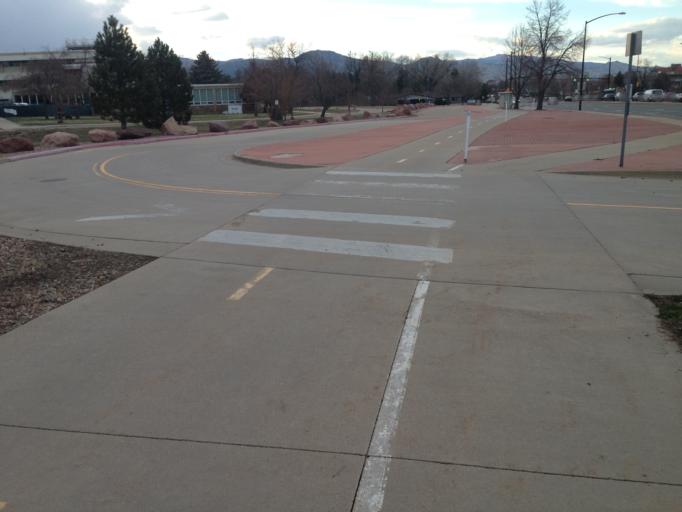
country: US
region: Colorado
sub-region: Boulder County
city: Boulder
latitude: 39.9951
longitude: -105.2604
